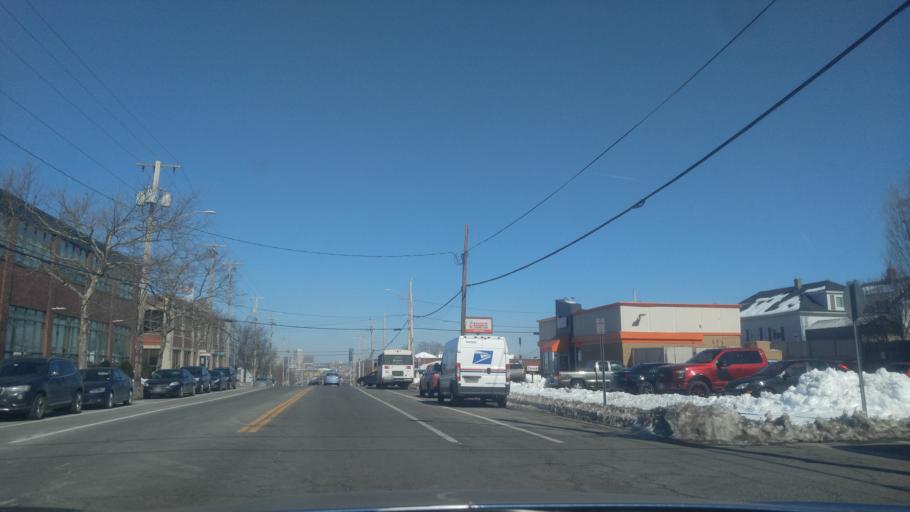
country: US
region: Rhode Island
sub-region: Providence County
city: East Providence
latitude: 41.7922
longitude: -71.3970
